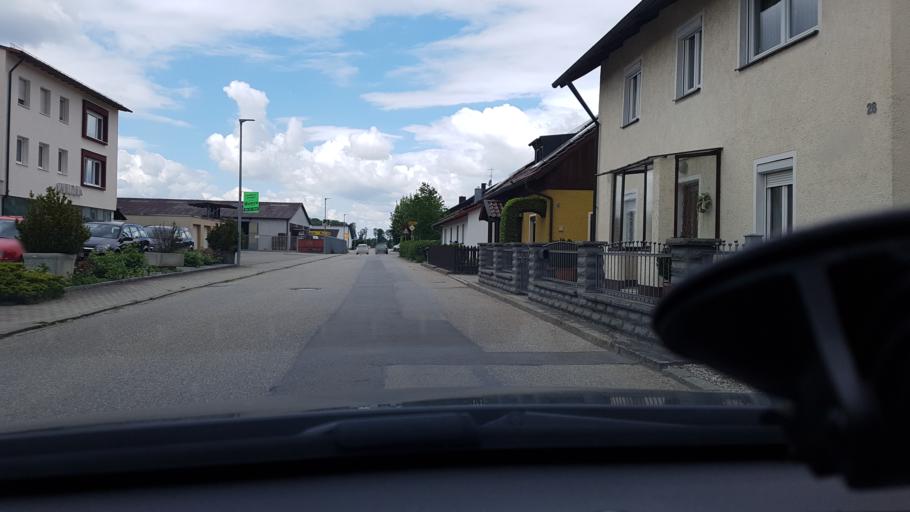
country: AT
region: Upper Austria
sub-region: Politischer Bezirk Scharding
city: Sankt Florian am Inn
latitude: 48.4048
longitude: 13.3840
